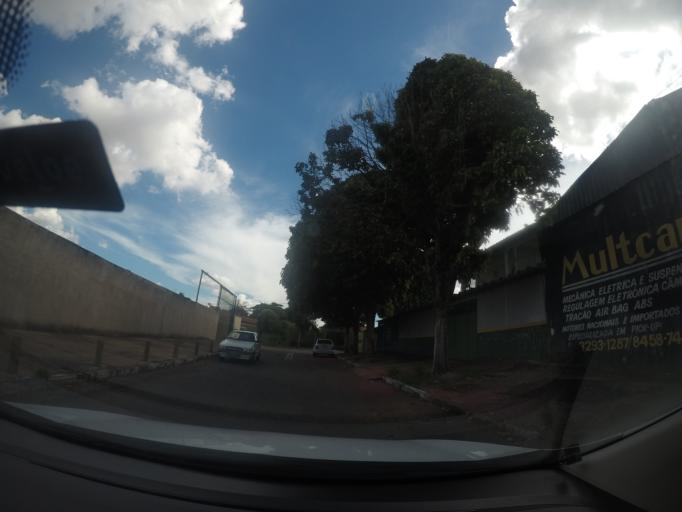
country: BR
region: Goias
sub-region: Goiania
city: Goiania
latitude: -16.6767
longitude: -49.3028
